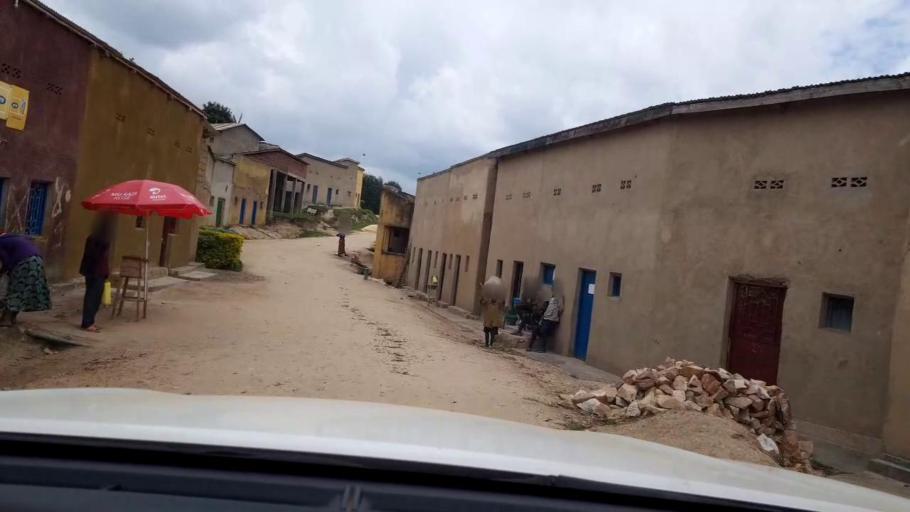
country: RW
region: Western Province
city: Kibuye
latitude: -1.8344
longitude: 29.5454
